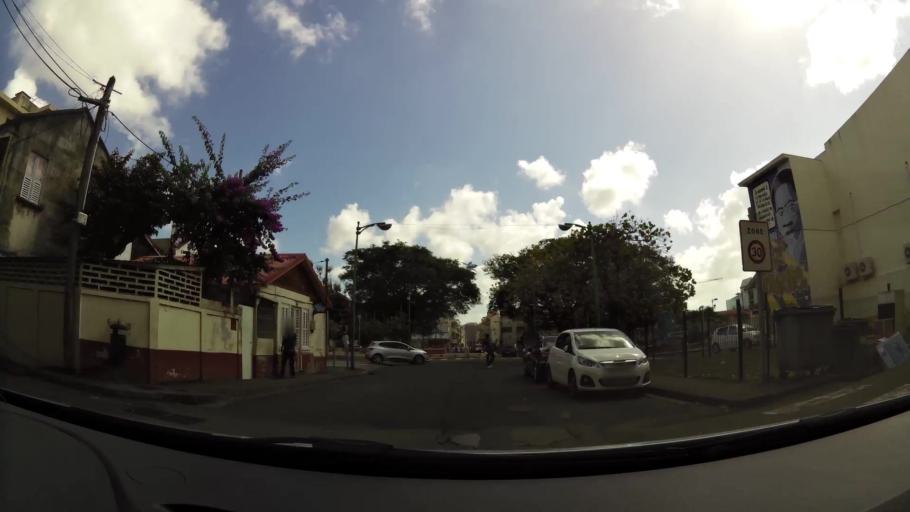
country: MQ
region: Martinique
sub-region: Martinique
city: Fort-de-France
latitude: 14.6120
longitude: -61.0716
